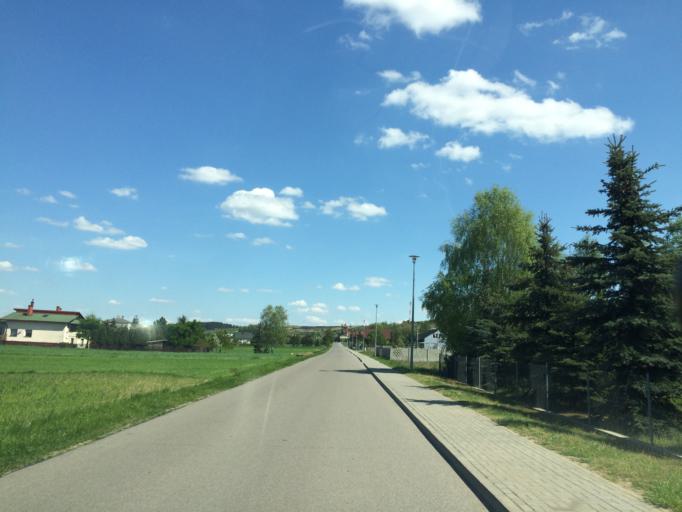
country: PL
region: Warmian-Masurian Voivodeship
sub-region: Powiat nowomiejski
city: Kurzetnik
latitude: 53.3969
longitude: 19.5622
